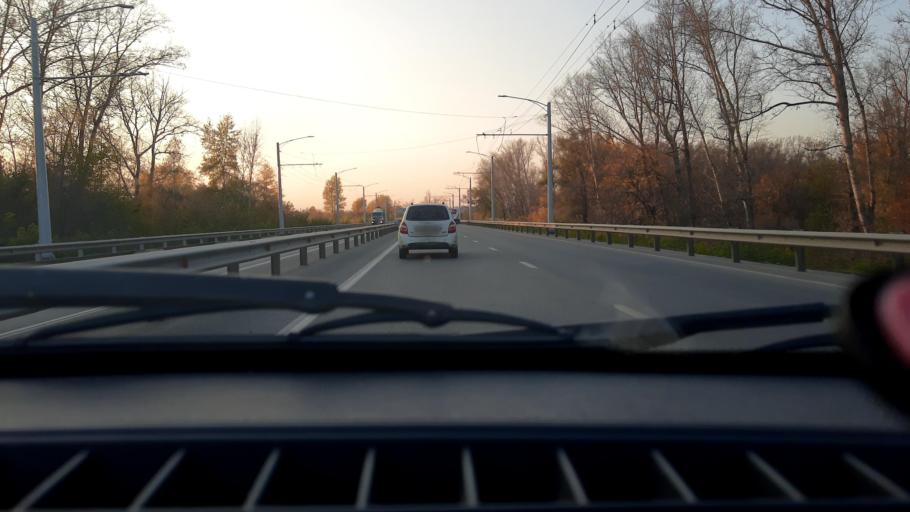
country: RU
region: Bashkortostan
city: Mikhaylovka
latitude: 54.7752
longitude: 55.8993
